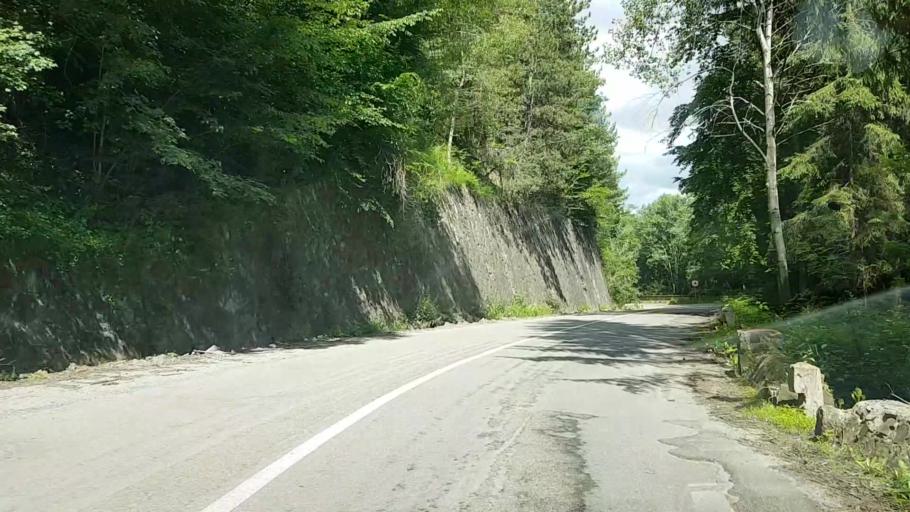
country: RO
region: Neamt
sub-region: Comuna Ceahlau
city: Ceahlau
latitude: 47.0527
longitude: 25.9866
